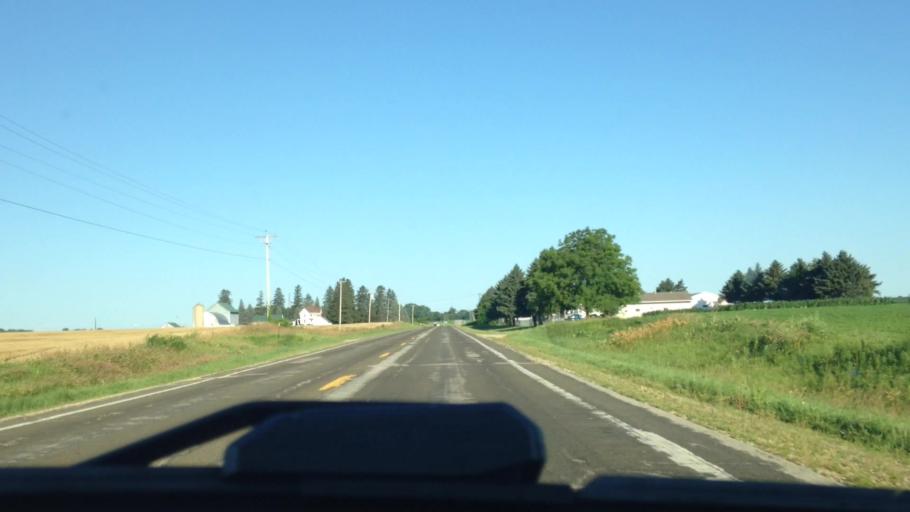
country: US
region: Wisconsin
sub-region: Columbia County
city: Poynette
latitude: 43.3378
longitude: -89.4362
